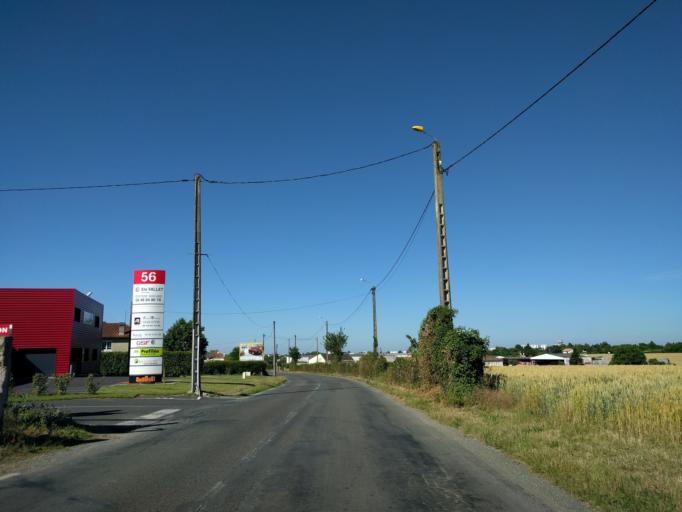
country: FR
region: Poitou-Charentes
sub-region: Departement des Deux-Sevres
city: Niort
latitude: 46.3390
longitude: -0.4208
